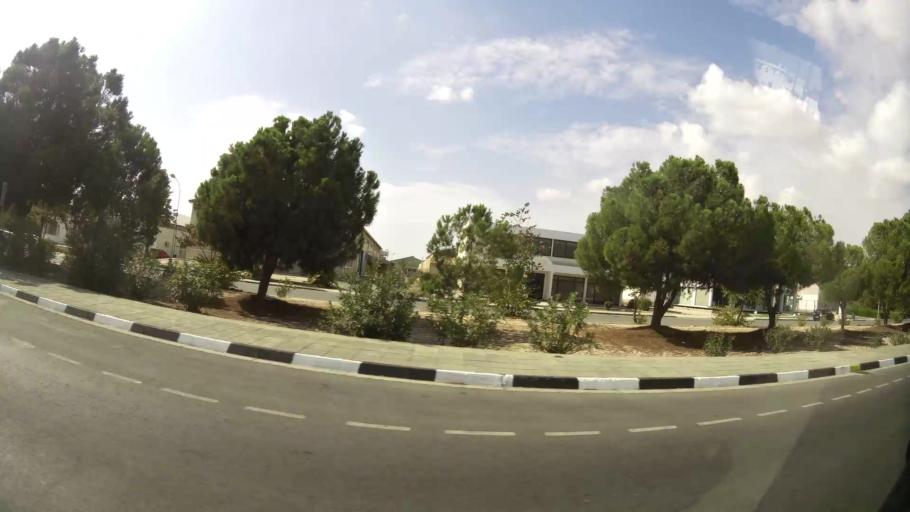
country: CY
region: Larnaka
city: Aradippou
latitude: 34.9385
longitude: 33.5880
